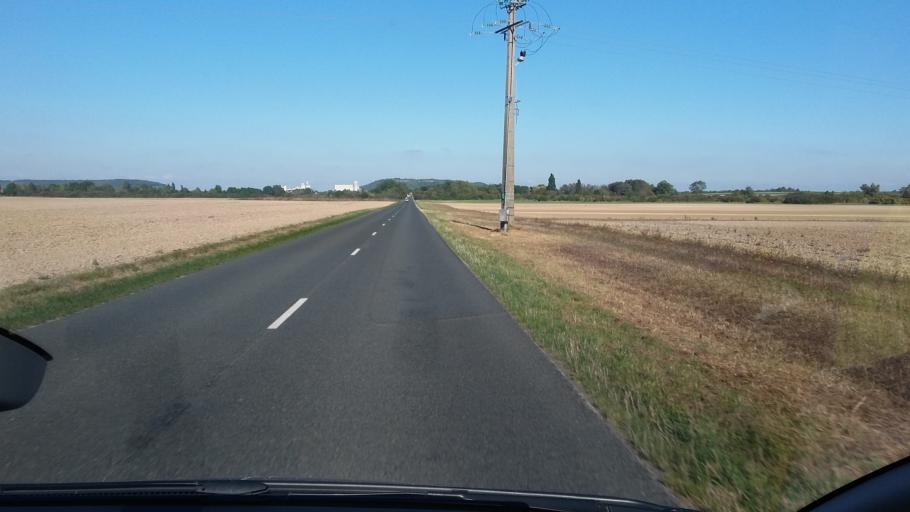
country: FR
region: Champagne-Ardenne
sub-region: Departement de la Marne
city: Fere-Champenoise
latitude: 48.8305
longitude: 3.9419
